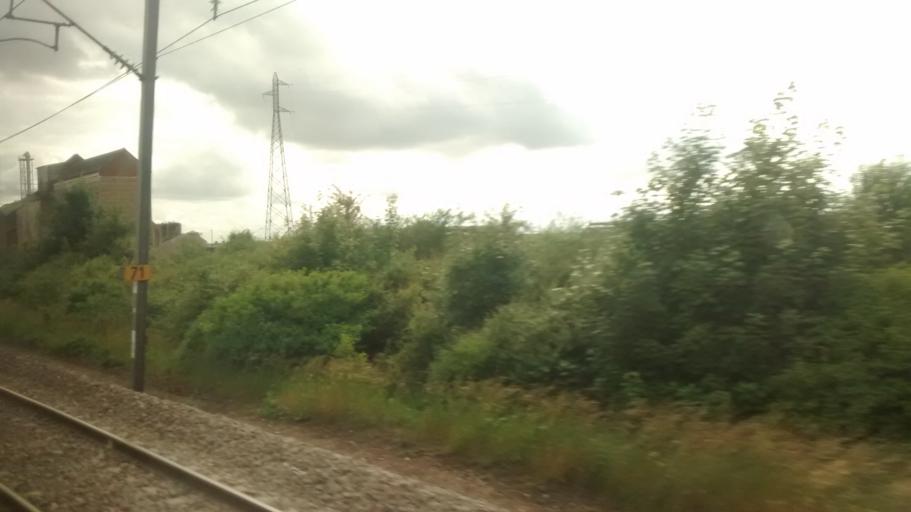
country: FR
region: Centre
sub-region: Departement d'Eure-et-Loir
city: Beville-le-Comte
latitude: 48.3935
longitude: 1.7334
